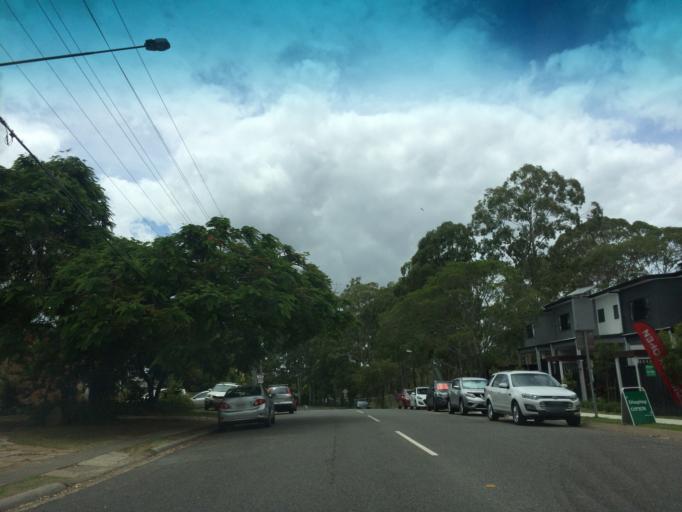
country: AU
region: Queensland
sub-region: Brisbane
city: Kenmore Hills
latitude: -27.5191
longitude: 152.9442
